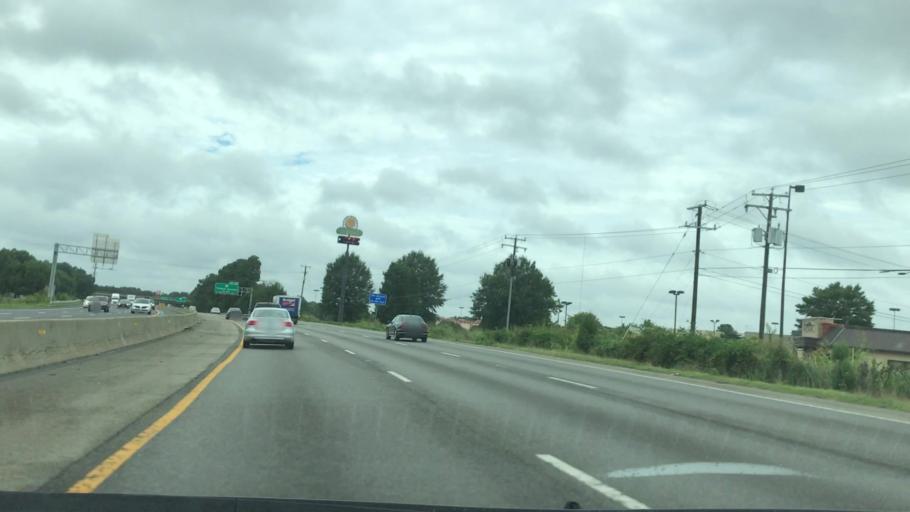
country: US
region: Virginia
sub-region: City of Colonial Heights
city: Colonial Heights
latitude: 37.2497
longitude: -77.3937
